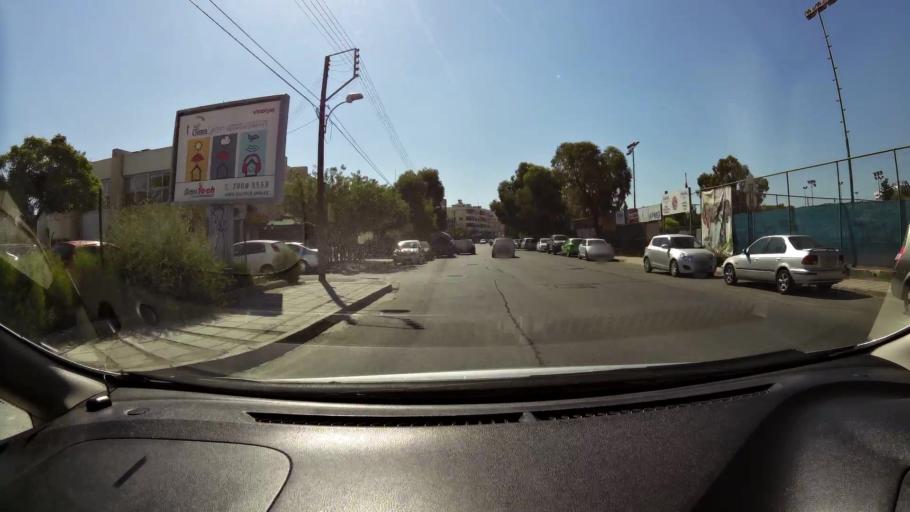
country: CY
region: Larnaka
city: Larnaca
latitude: 34.9212
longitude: 33.6337
